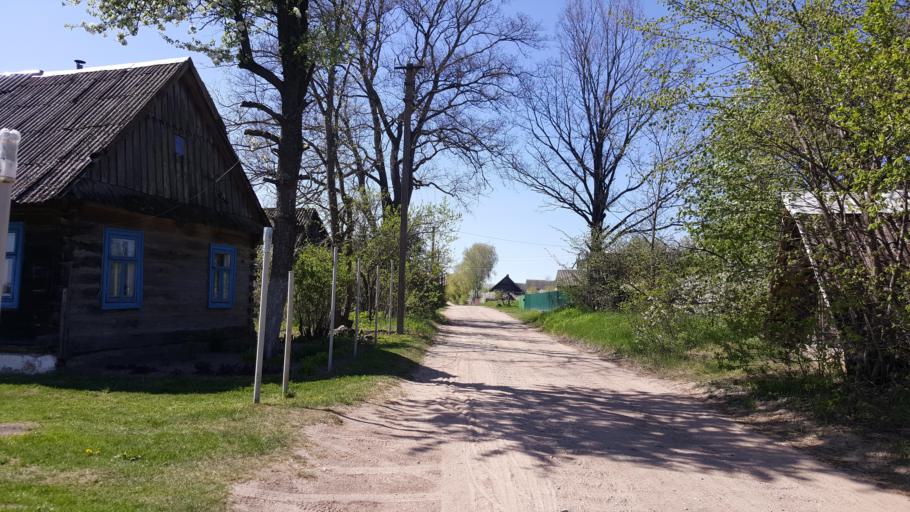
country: BY
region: Brest
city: Kamyanyets
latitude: 52.4528
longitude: 23.8865
